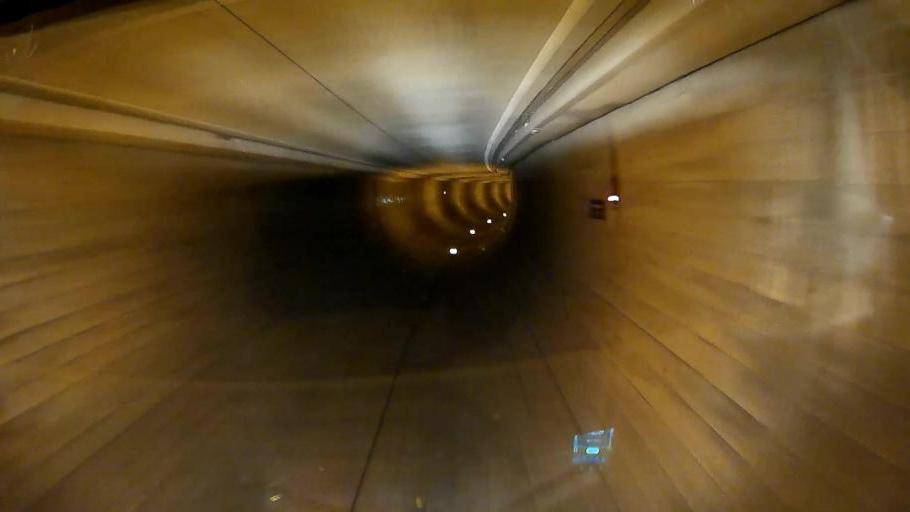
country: JP
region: Shizuoka
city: Shizuoka-shi
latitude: 35.2773
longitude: 138.2188
